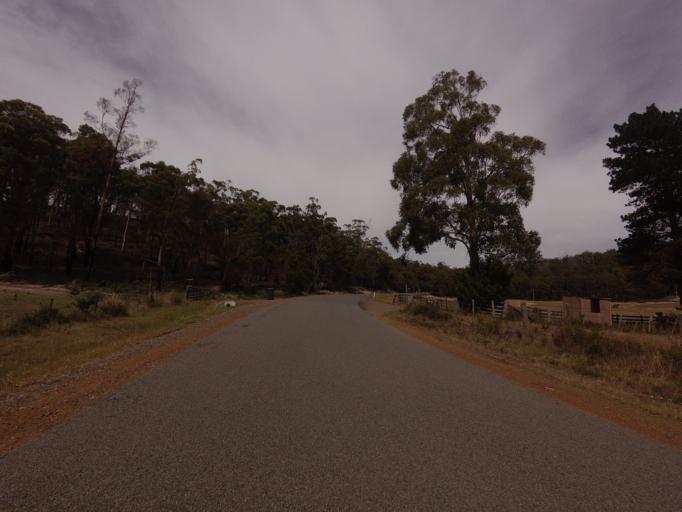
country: AU
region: Tasmania
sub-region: Sorell
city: Sorell
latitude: -42.5787
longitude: 147.5597
